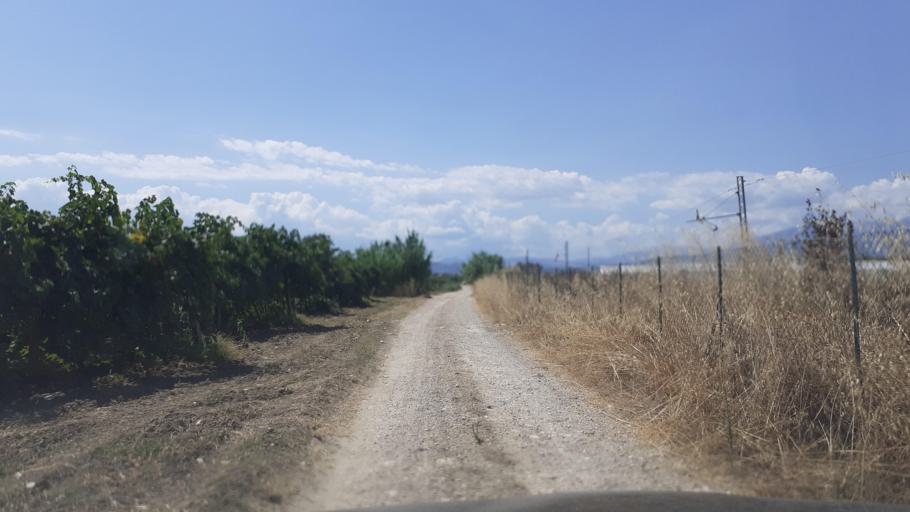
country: IT
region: Abruzzo
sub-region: Provincia di Chieti
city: Fossacesia
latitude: 42.2069
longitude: 14.4933
